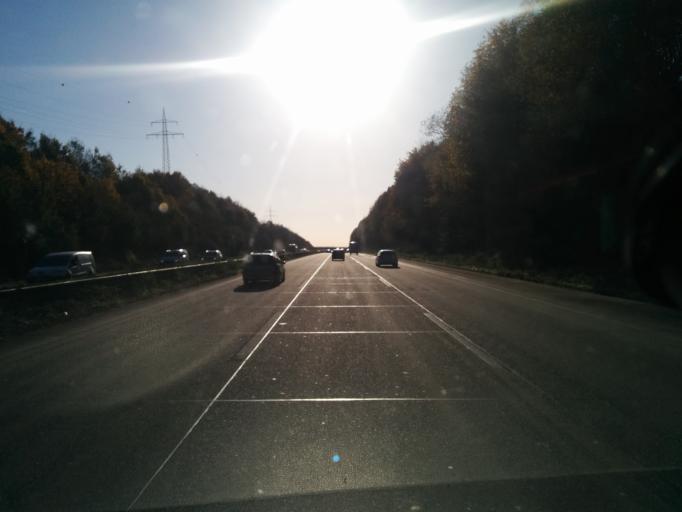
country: DE
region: North Rhine-Westphalia
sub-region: Regierungsbezirk Dusseldorf
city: Erkrath
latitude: 51.2172
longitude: 6.9235
